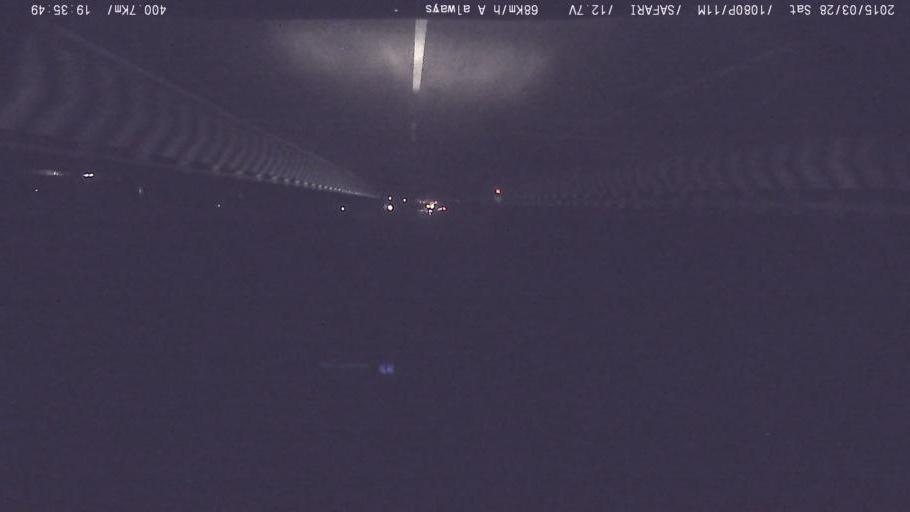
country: IN
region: Karnataka
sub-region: Mandya
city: Shrirangapattana
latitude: 12.4318
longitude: 76.7059
